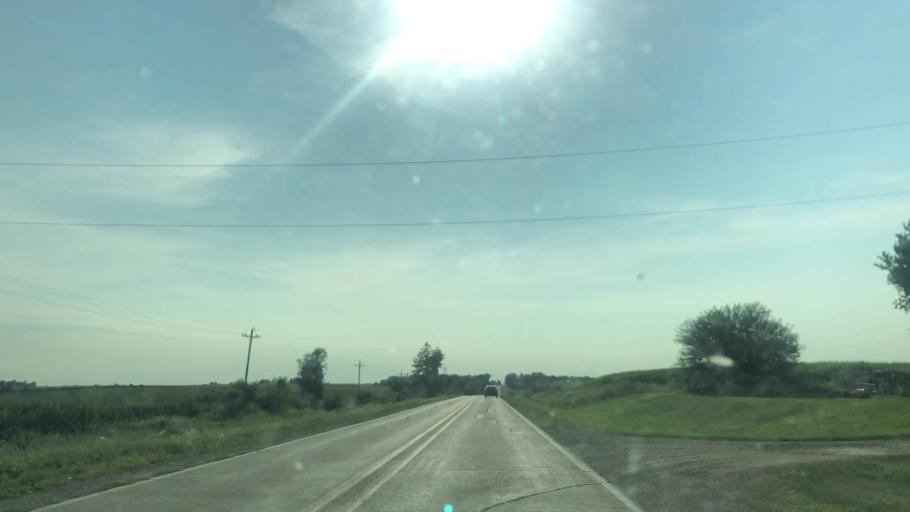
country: US
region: Iowa
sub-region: Marshall County
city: Marshalltown
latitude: 42.0489
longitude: -92.9933
